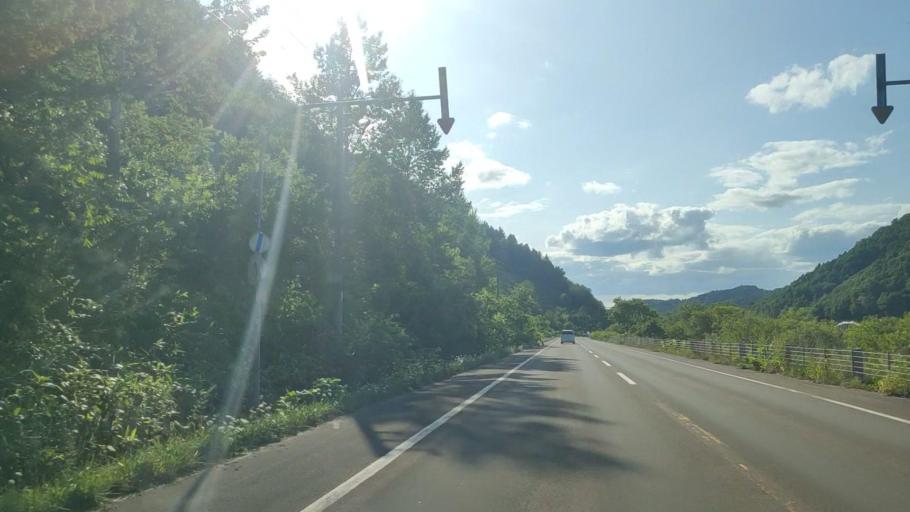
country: JP
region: Hokkaido
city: Nayoro
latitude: 44.7297
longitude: 142.1016
